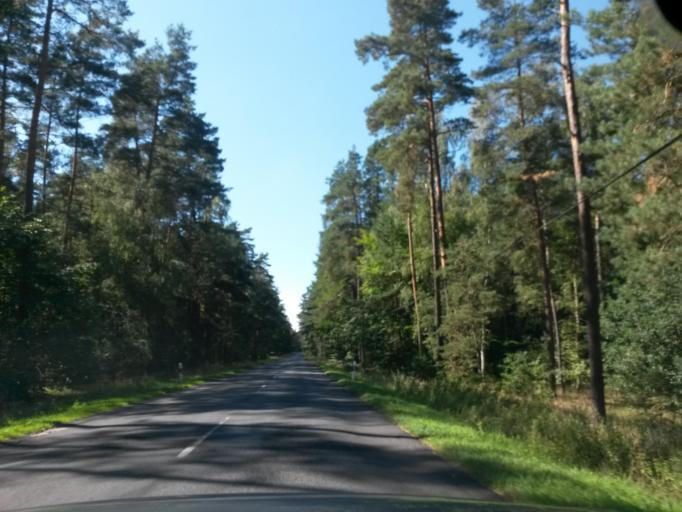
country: DE
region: Brandenburg
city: Lychen
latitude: 53.2235
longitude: 13.3549
